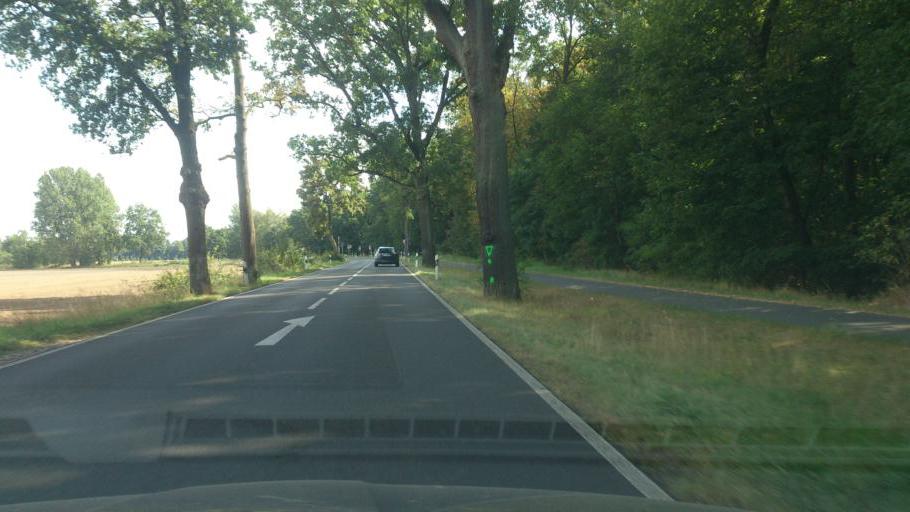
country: DE
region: Brandenburg
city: Stahnsdorf
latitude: 52.3372
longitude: 13.1604
